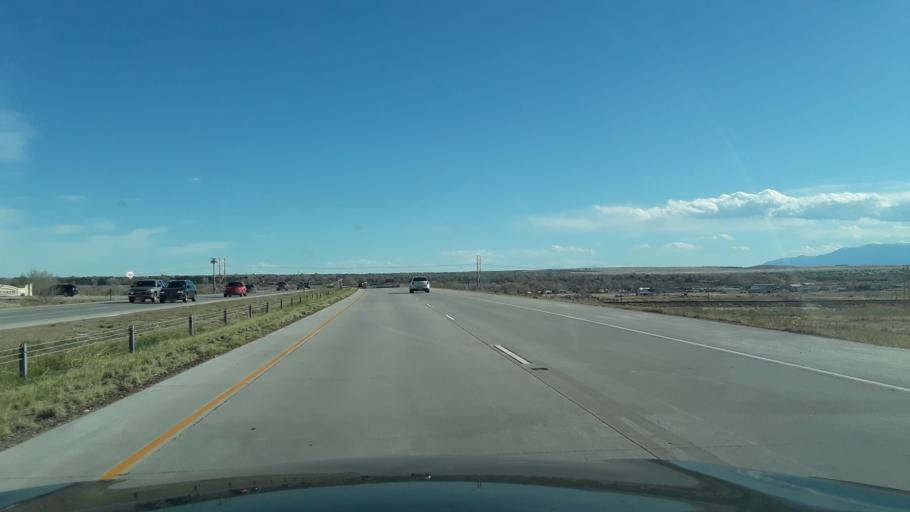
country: US
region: Colorado
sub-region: Pueblo County
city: Pueblo
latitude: 38.2855
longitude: -104.6633
